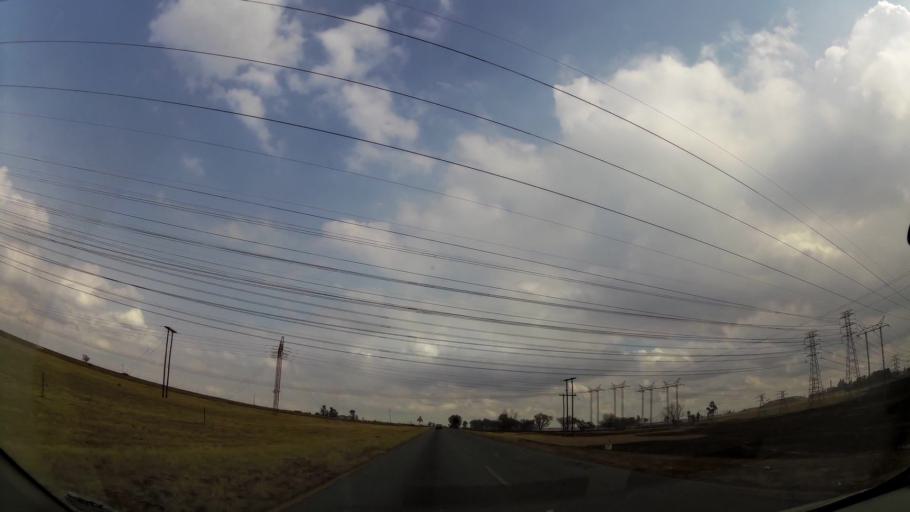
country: ZA
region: Orange Free State
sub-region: Fezile Dabi District Municipality
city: Sasolburg
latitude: -26.8265
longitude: 27.9012
